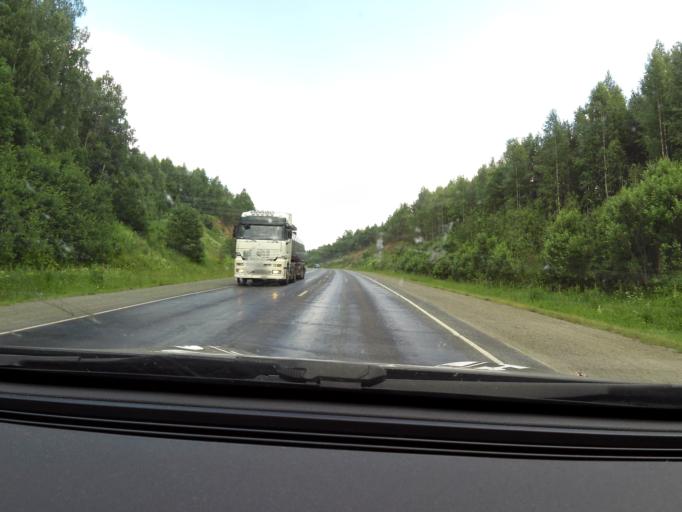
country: RU
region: Sverdlovsk
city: Bisert'
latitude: 56.8355
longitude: 58.8845
